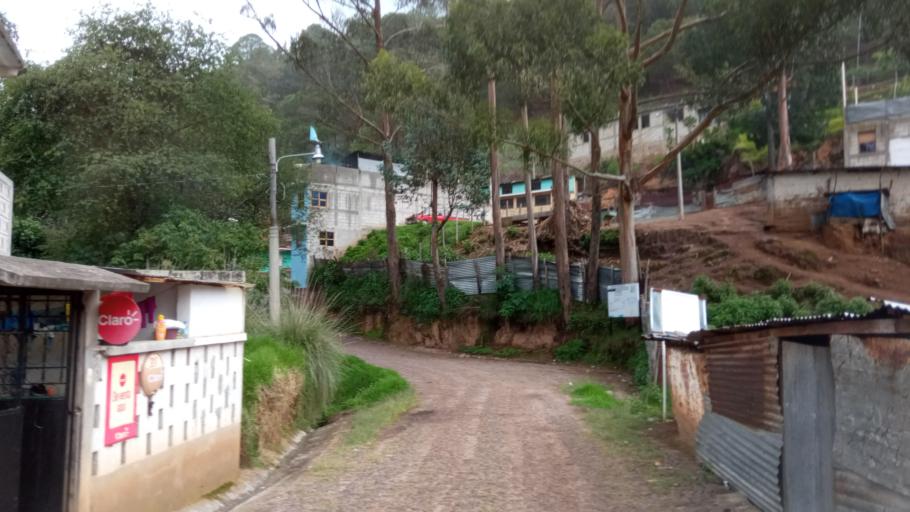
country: GT
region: San Marcos
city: Tejutla
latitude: 15.1191
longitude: -91.8036
